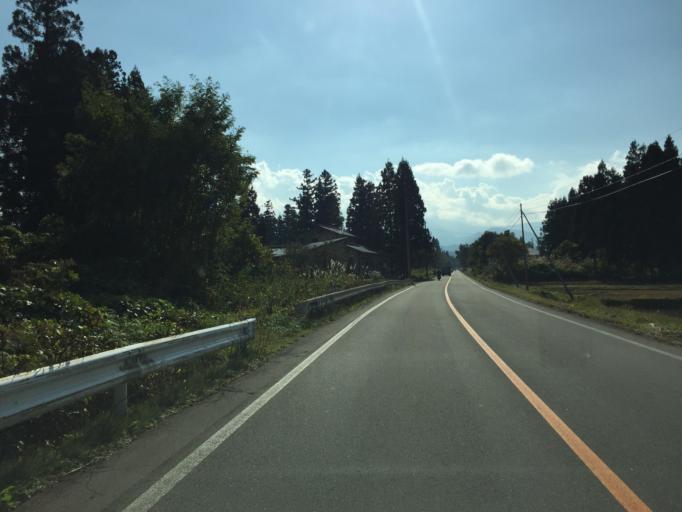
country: JP
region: Yamagata
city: Yonezawa
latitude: 37.9022
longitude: 140.0249
